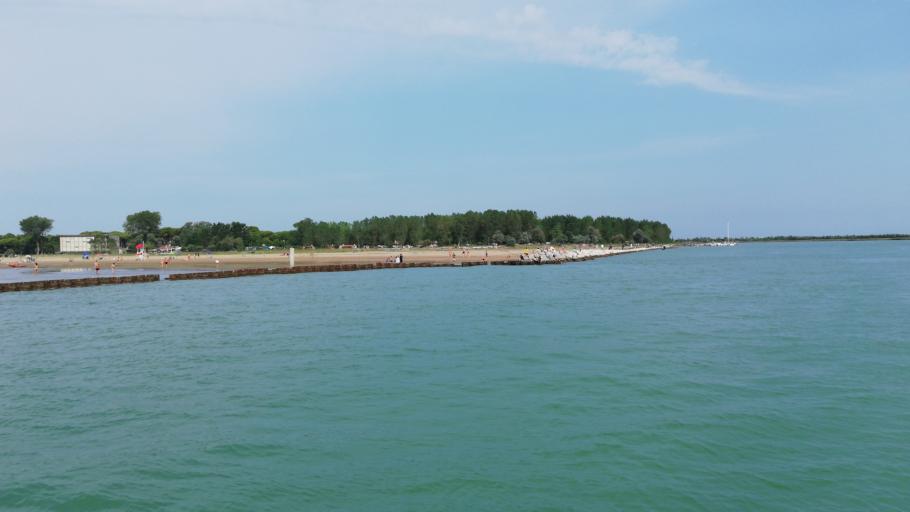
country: IT
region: Veneto
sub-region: Provincia di Venezia
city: Caorle
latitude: 45.6130
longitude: 12.9124
